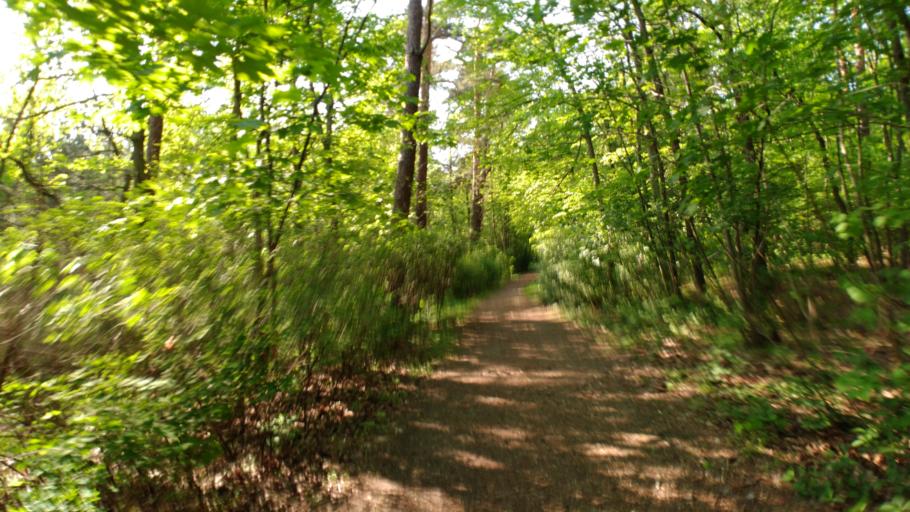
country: DE
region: Saxony
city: Albertstadt
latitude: 51.0760
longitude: 13.7908
